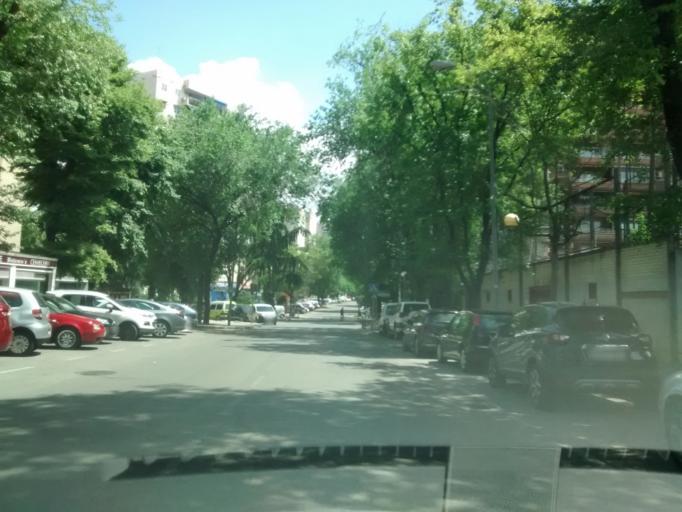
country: ES
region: Madrid
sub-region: Provincia de Madrid
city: San Fernando de Henares
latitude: 40.4305
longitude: -3.5421
